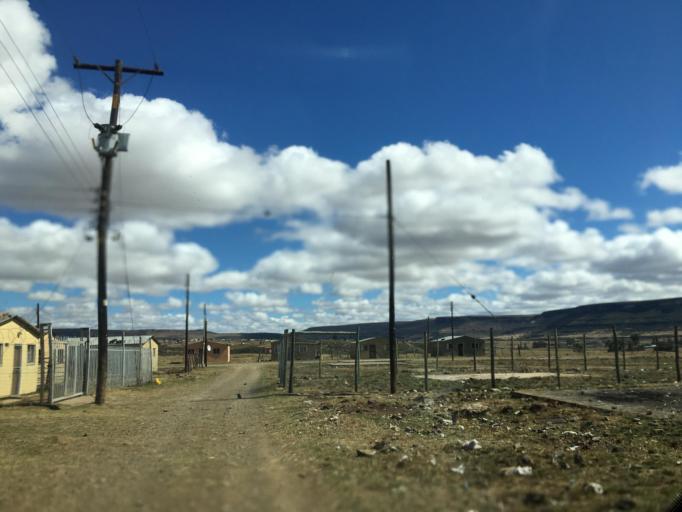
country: ZA
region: Eastern Cape
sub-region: Chris Hani District Municipality
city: Cala
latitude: -31.5398
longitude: 27.6793
